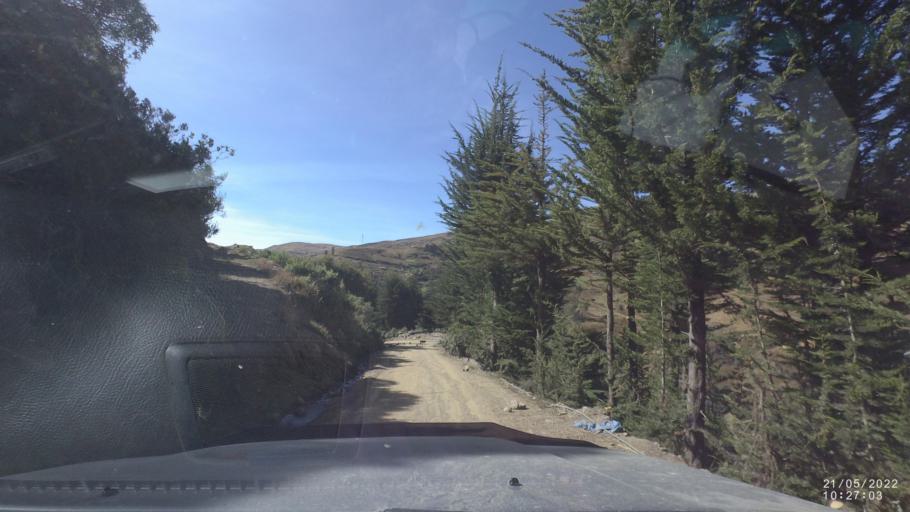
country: BO
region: Cochabamba
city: Colomi
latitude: -17.3231
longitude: -65.9449
